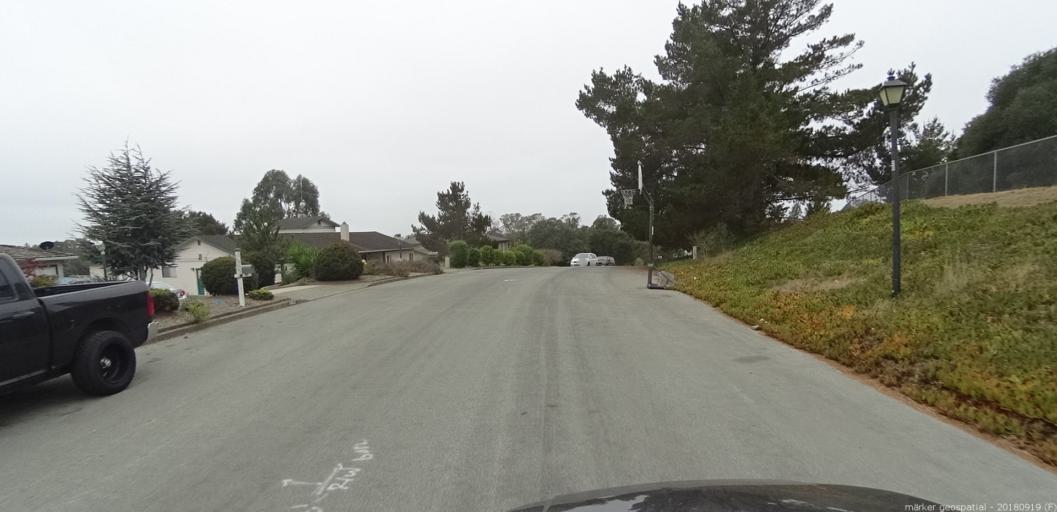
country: US
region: California
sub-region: Monterey County
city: Castroville
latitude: 36.7817
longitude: -121.7181
